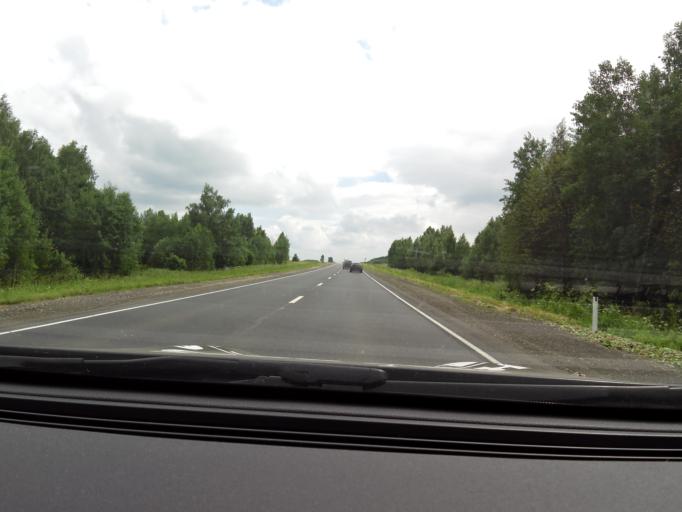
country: RU
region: Perm
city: Orda
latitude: 57.2490
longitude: 57.0429
